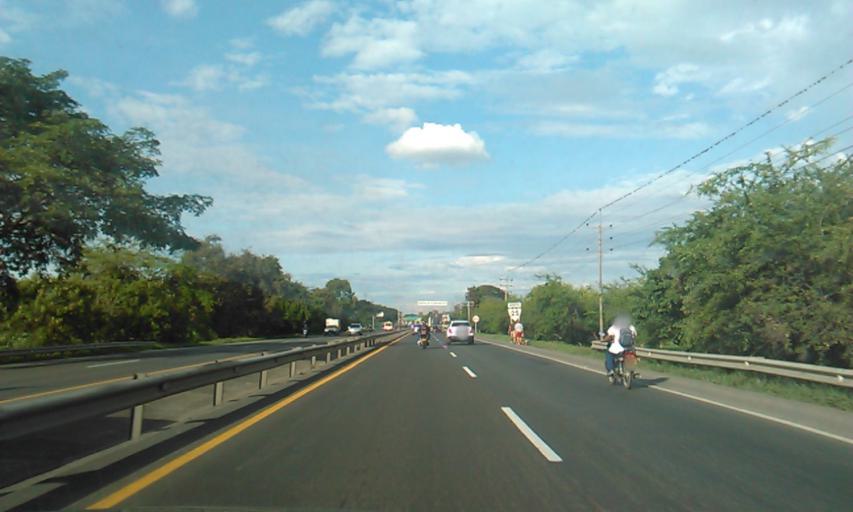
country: CO
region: Valle del Cauca
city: Buga
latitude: 3.9058
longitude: -76.3091
